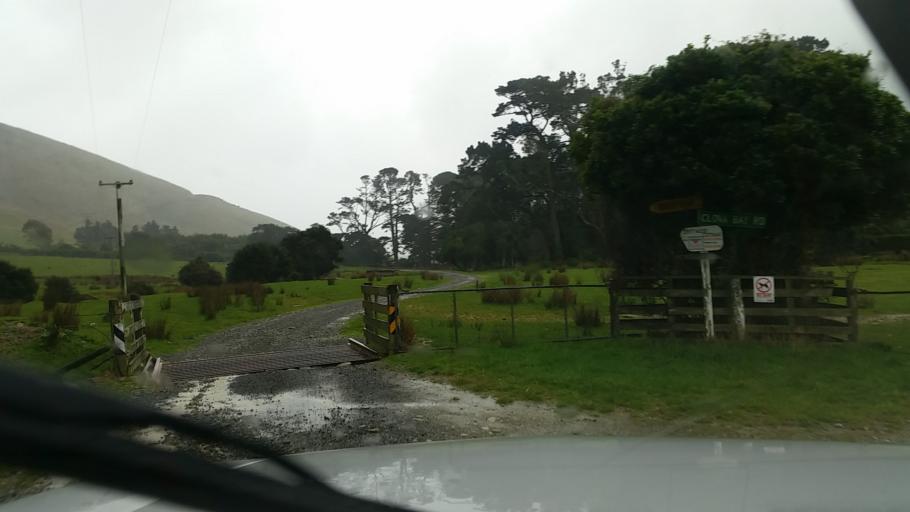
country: NZ
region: Marlborough
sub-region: Marlborough District
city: Picton
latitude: -41.1162
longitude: 174.0361
